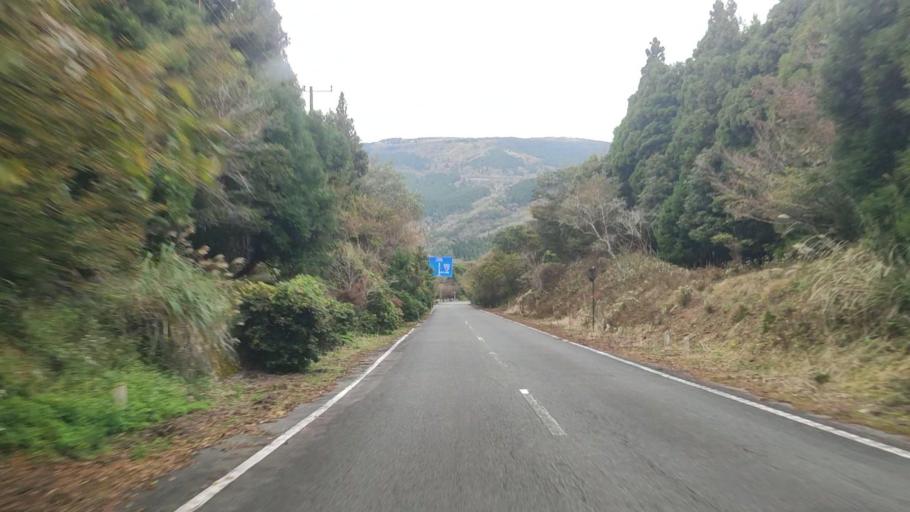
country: JP
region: Shizuoka
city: Heda
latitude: 34.9176
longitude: 138.8422
